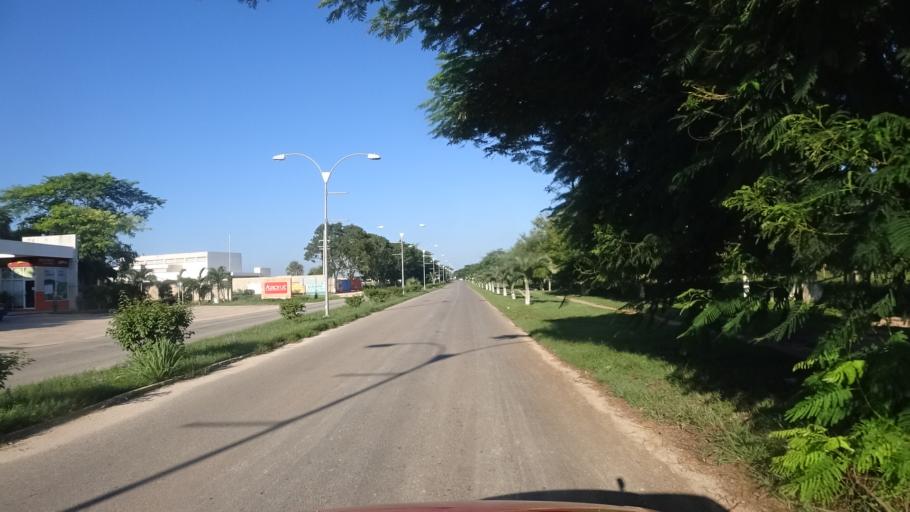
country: MX
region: Yucatan
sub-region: Tizimin
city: Tizimin
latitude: 21.1522
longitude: -88.1742
